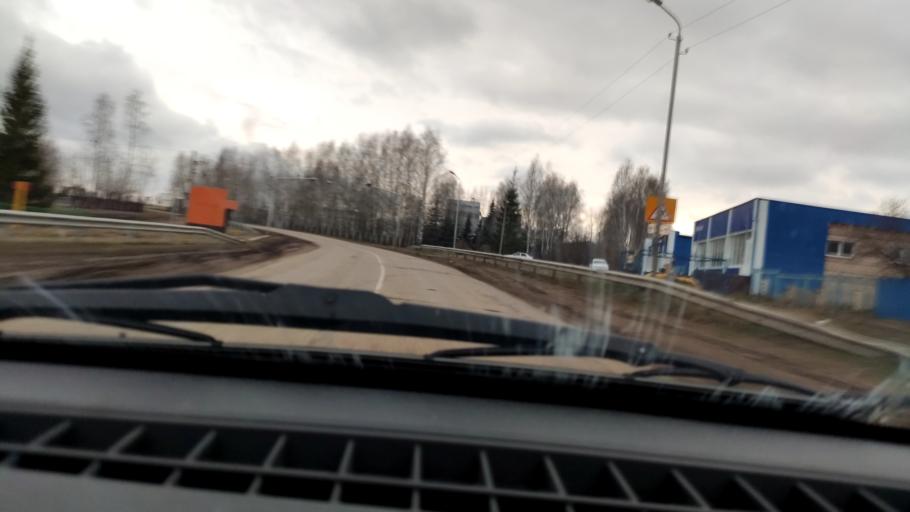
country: RU
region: Bashkortostan
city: Chekmagush
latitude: 55.1177
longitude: 54.4268
